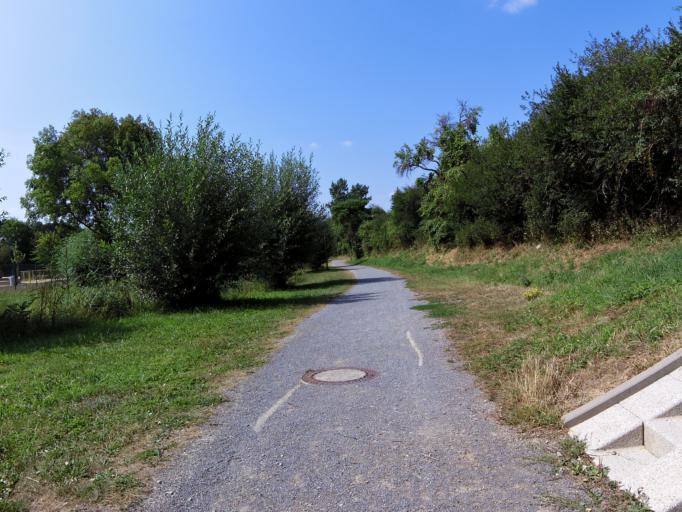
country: DE
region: Bavaria
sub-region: Regierungsbezirk Unterfranken
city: Estenfeld
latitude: 49.8272
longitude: 10.0155
